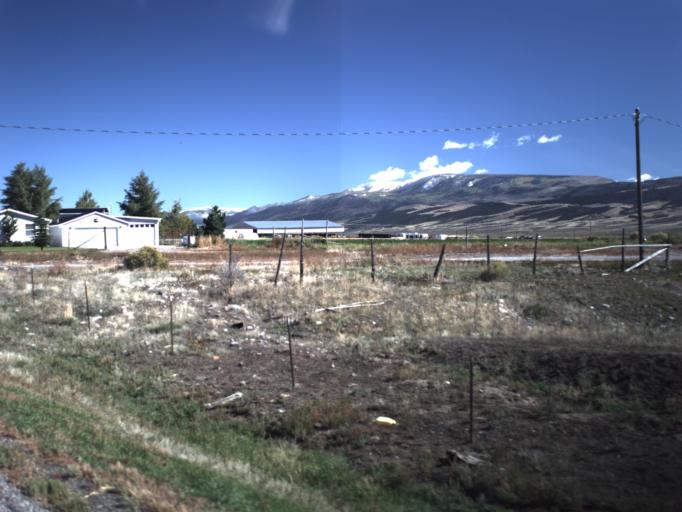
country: US
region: Utah
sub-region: Wayne County
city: Loa
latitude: 38.4300
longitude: -111.9226
